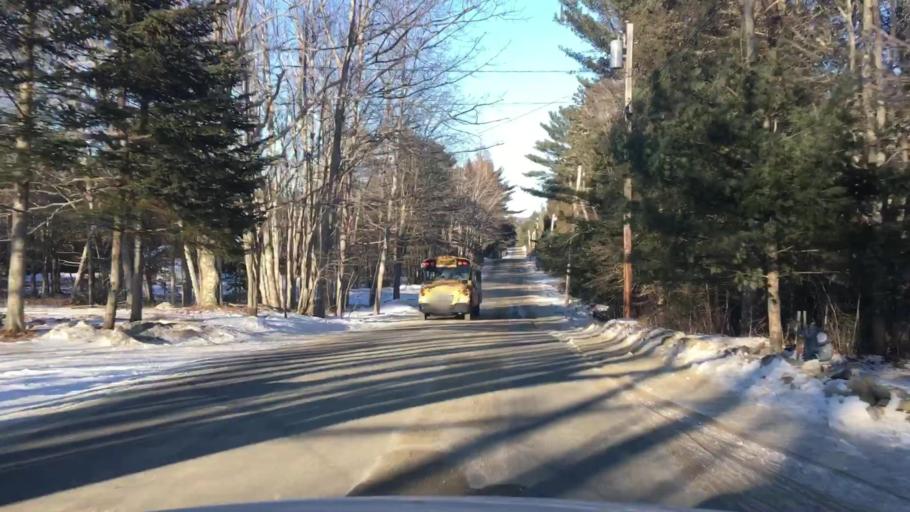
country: US
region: Maine
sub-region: Hancock County
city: Penobscot
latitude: 44.3889
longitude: -68.7166
